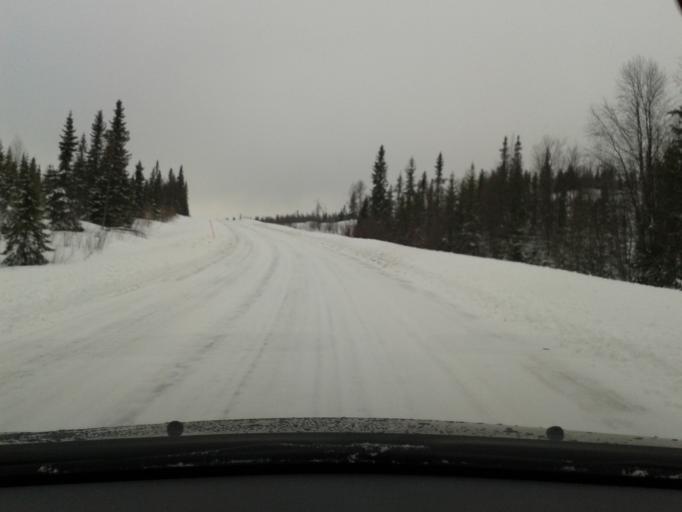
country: SE
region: Vaesterbotten
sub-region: Vilhelmina Kommun
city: Sjoberg
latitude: 65.2034
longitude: 15.9782
